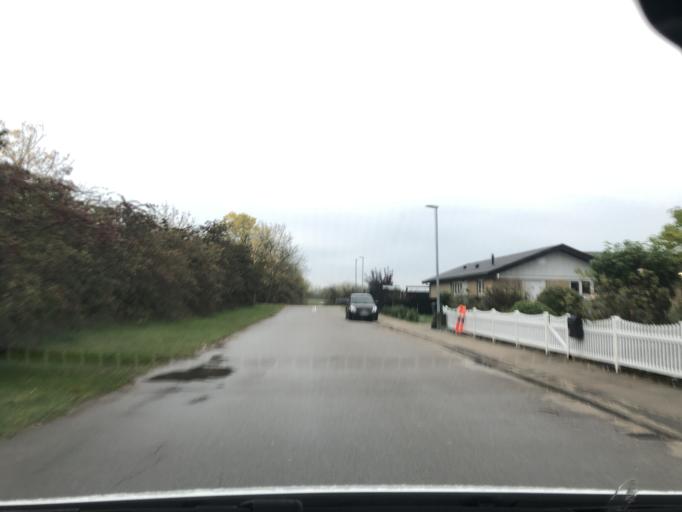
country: DK
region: Capital Region
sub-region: Tarnby Kommune
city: Tarnby
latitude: 55.5931
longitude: 12.5907
